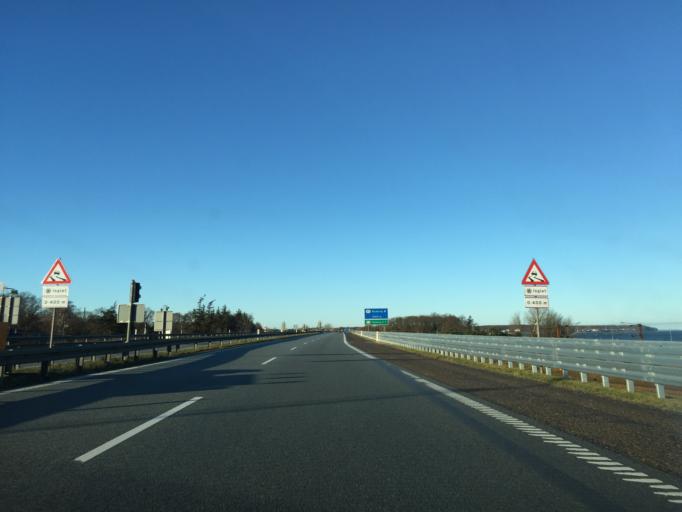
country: DK
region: South Denmark
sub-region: Nyborg Kommune
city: Nyborg
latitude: 55.3005
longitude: 10.8321
